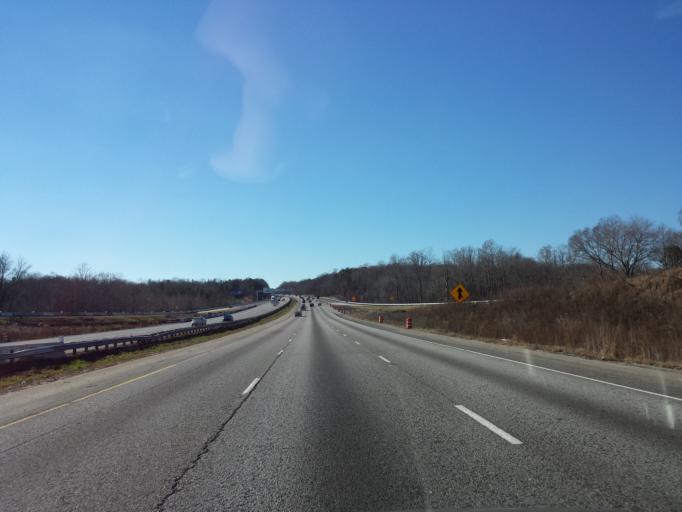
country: US
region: Georgia
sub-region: Douglas County
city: Lithia Springs
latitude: 33.7686
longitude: -84.6527
